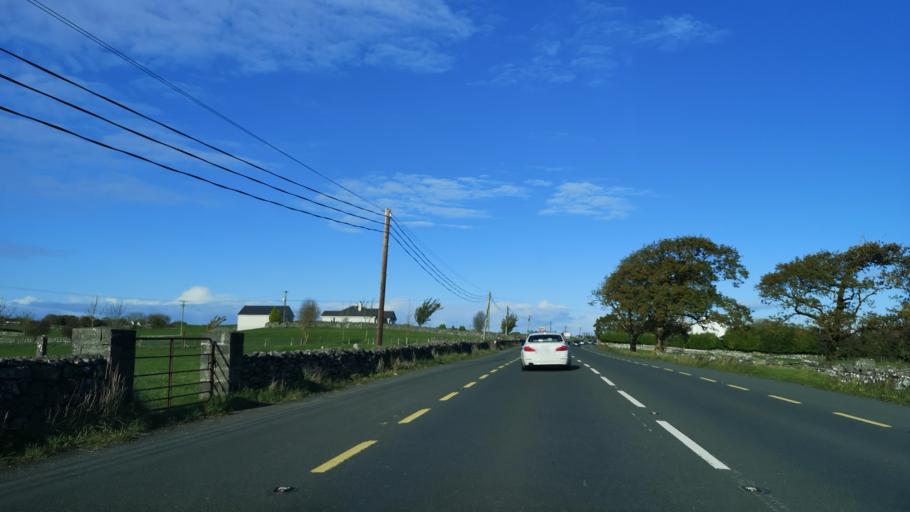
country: IE
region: Connaught
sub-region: County Galway
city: Moycullen
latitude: 53.4558
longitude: -9.0977
